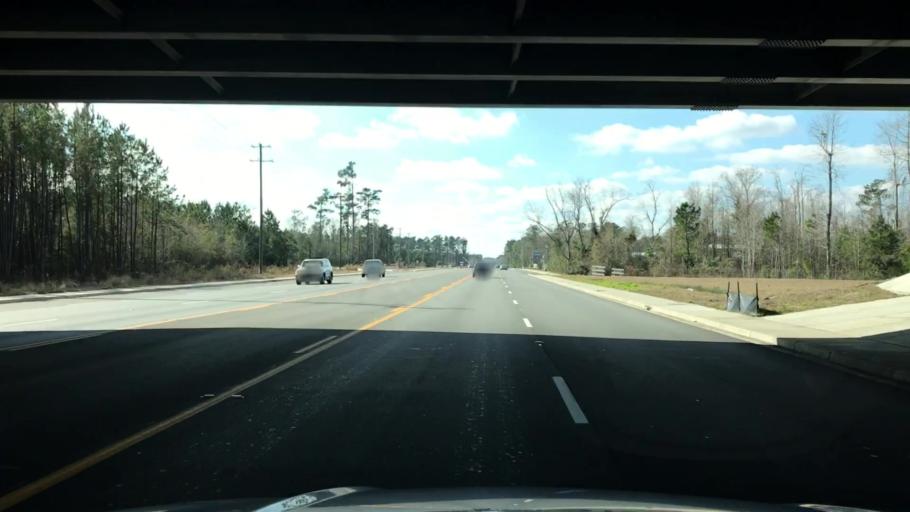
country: US
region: South Carolina
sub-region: Horry County
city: Socastee
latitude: 33.6534
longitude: -79.0194
